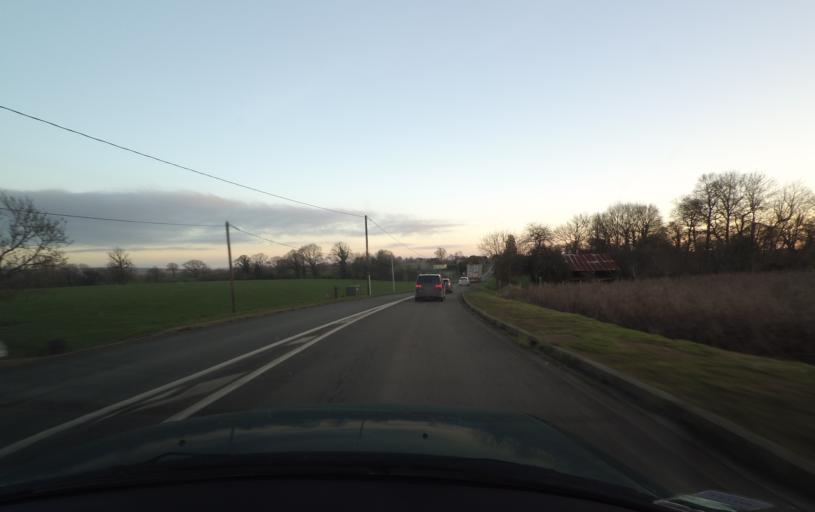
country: FR
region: Pays de la Loire
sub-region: Departement de la Mayenne
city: Bais
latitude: 48.2928
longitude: -0.3590
